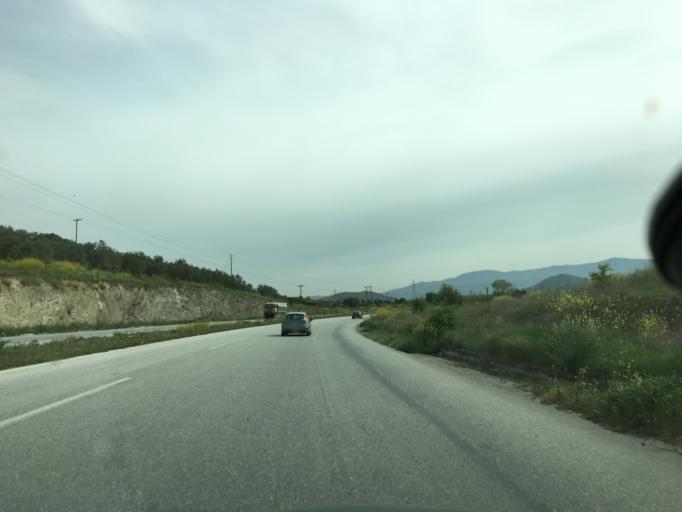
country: GR
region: Thessaly
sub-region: Nomos Magnisias
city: Velestino
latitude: 39.3825
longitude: 22.8326
